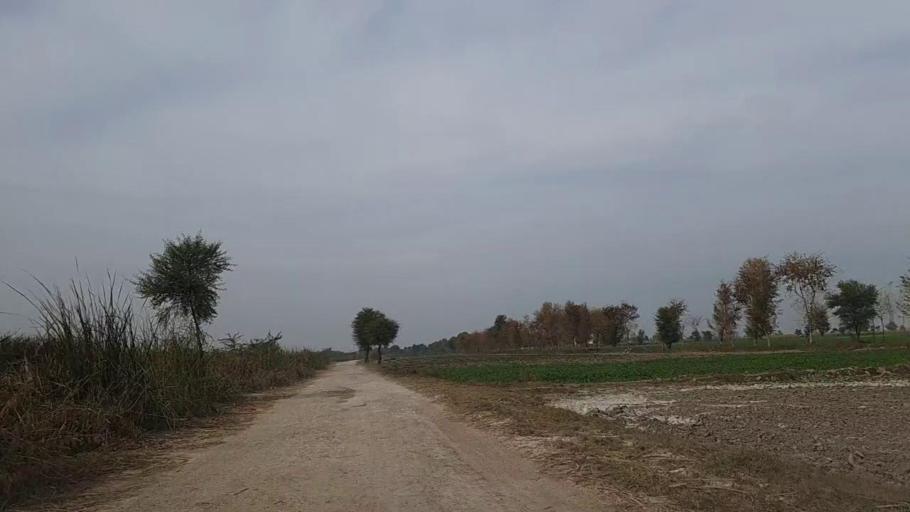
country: PK
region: Sindh
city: Daur
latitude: 26.4198
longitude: 68.4215
